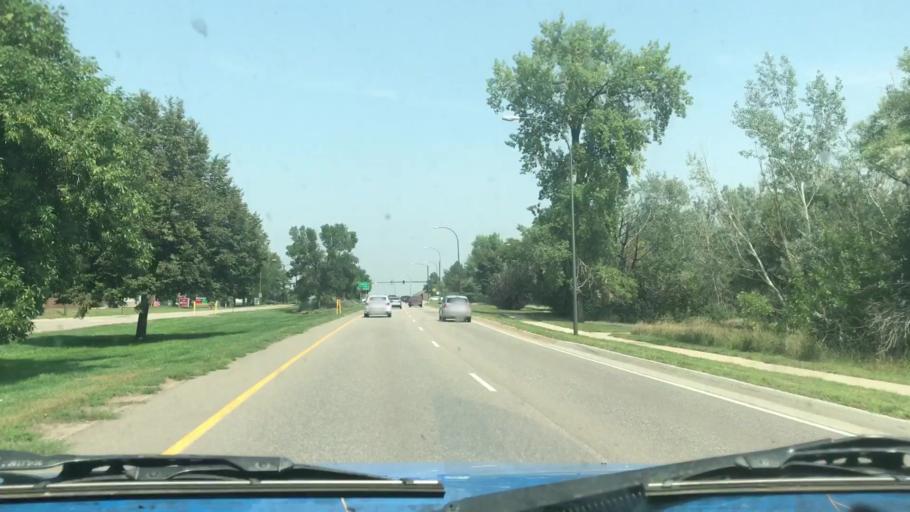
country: US
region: Colorado
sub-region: Jefferson County
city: Lakewood
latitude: 39.6887
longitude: -105.1195
